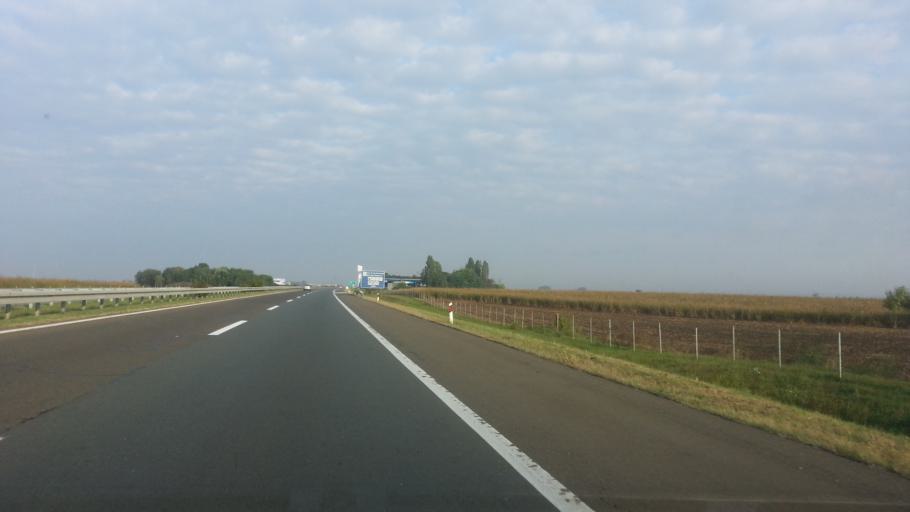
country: RS
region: Autonomna Pokrajina Vojvodina
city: Nova Pazova
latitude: 44.9679
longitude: 20.2379
